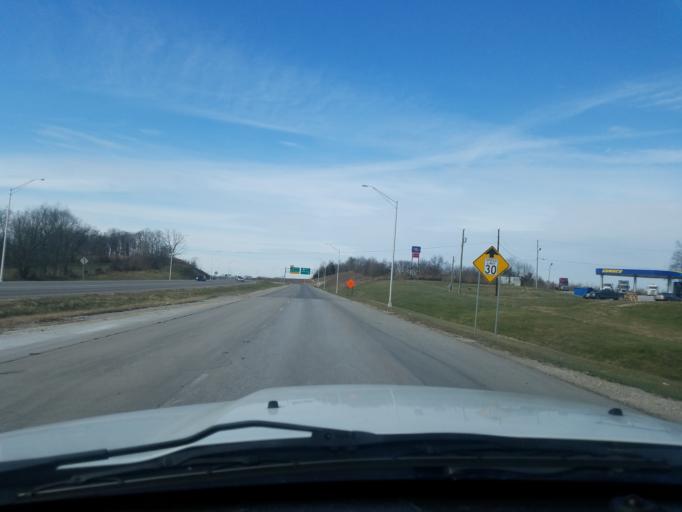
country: US
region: Indiana
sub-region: Monroe County
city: Bloomington
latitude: 39.1058
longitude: -86.5513
